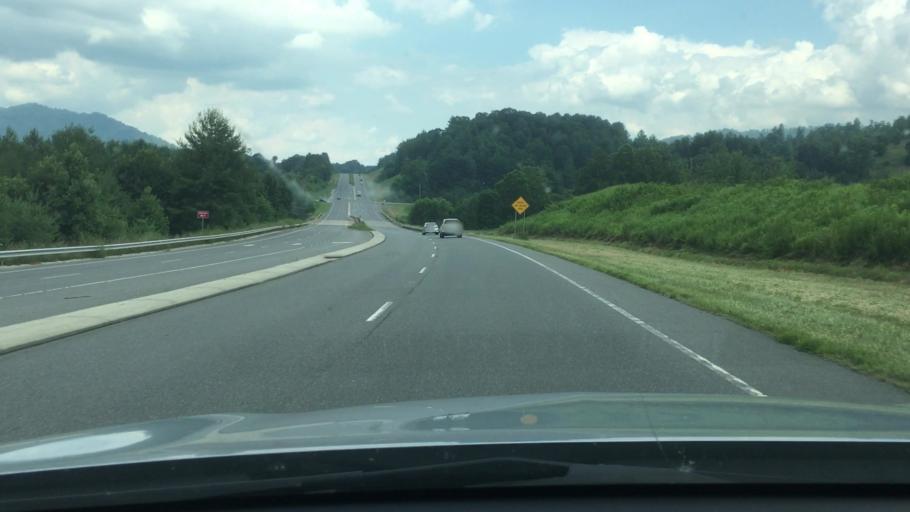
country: US
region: North Carolina
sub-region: Yancey County
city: Burnsville
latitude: 35.9106
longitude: -82.3866
